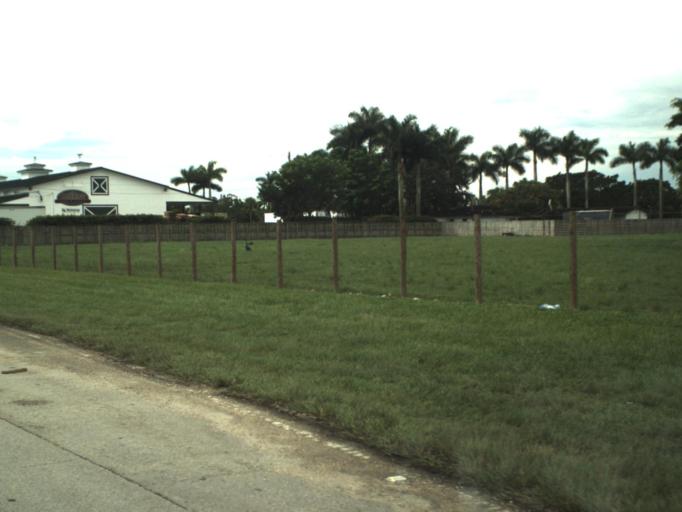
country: US
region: Florida
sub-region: Miami-Dade County
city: Naranja
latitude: 25.5596
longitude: -80.4782
